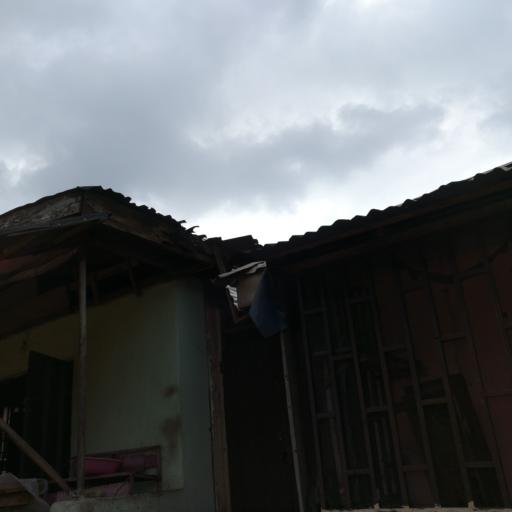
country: NG
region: Rivers
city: Port Harcourt
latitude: 4.8318
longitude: 7.0696
